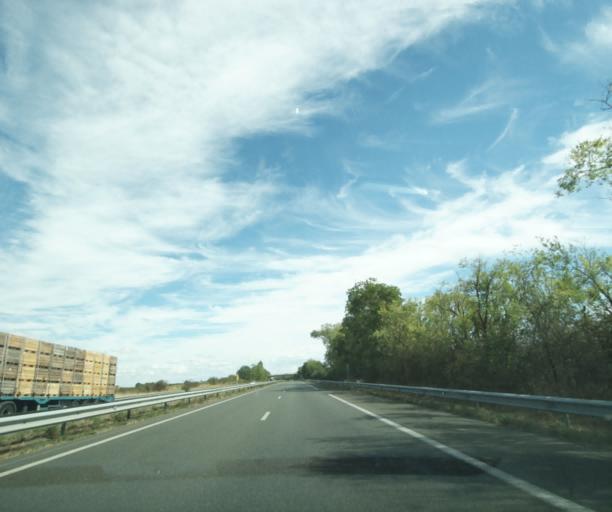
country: FR
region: Midi-Pyrenees
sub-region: Departement du Tarn-et-Garonne
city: Saint-Nicolas-de-la-Grave
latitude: 44.0405
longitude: 1.0227
